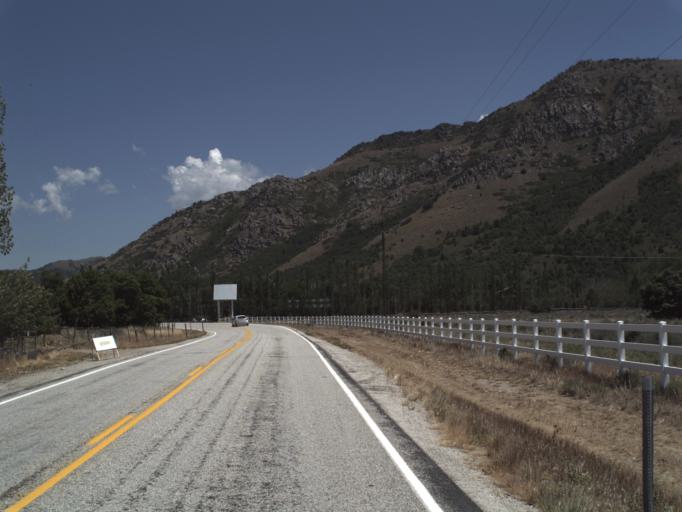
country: US
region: Utah
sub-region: Weber County
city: Wolf Creek
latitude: 41.2611
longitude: -111.7063
